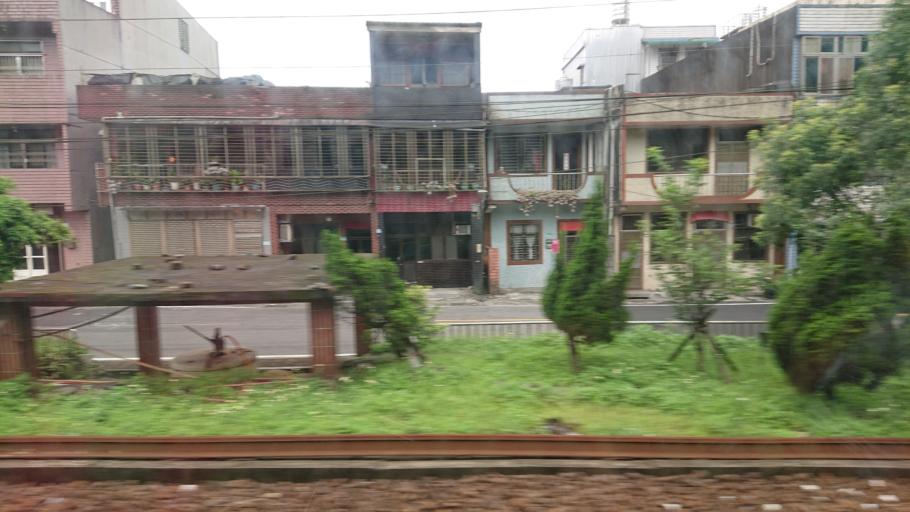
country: TW
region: Taiwan
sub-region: Keelung
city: Keelung
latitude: 25.1081
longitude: 121.8182
